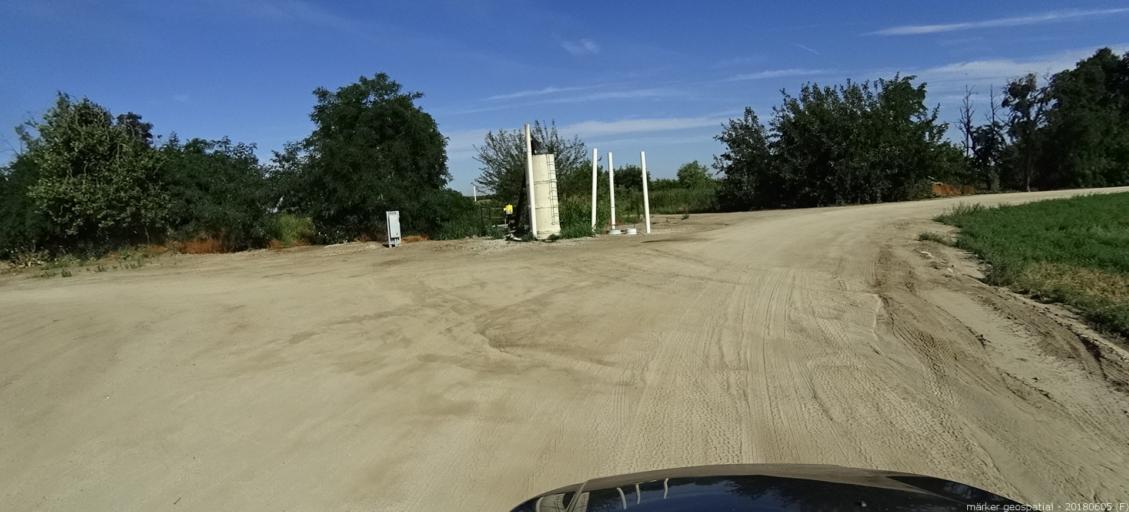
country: US
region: California
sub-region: Madera County
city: Chowchilla
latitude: 37.1418
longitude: -120.3027
